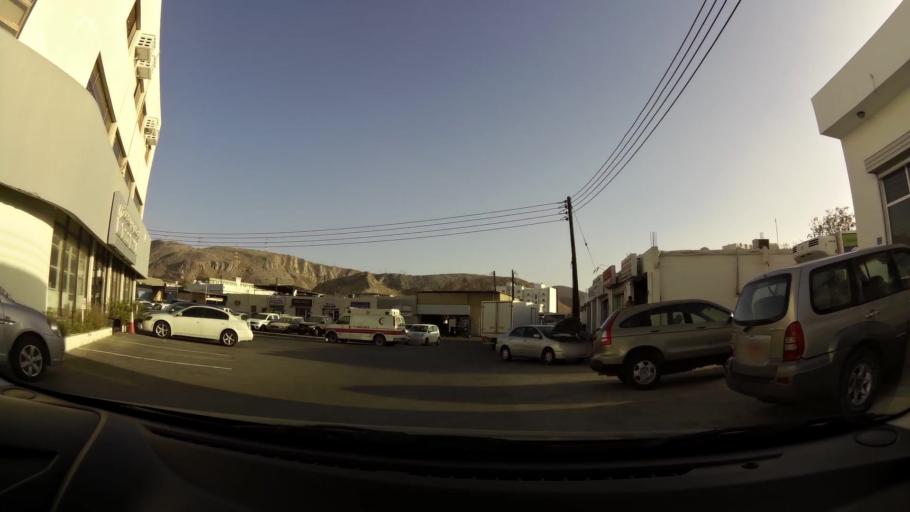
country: OM
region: Muhafazat Masqat
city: Muscat
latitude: 23.5899
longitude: 58.5549
